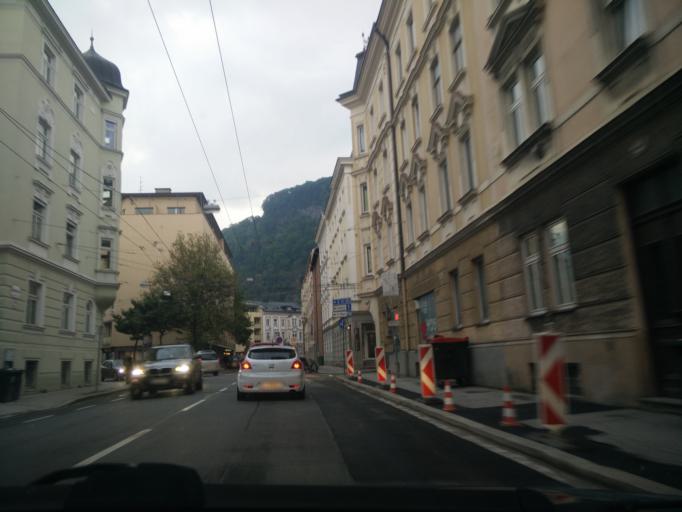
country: AT
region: Salzburg
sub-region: Salzburg Stadt
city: Salzburg
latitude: 47.8087
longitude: 13.0497
